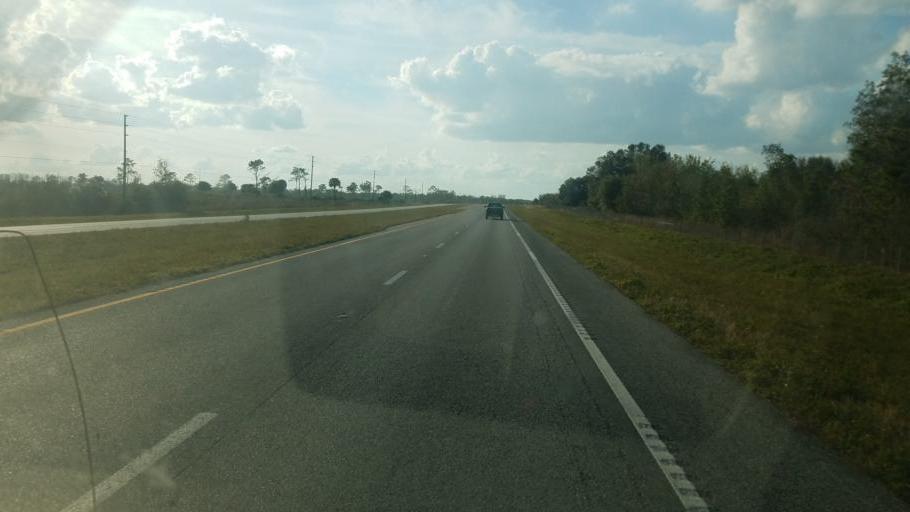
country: US
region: Florida
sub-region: Osceola County
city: Saint Cloud
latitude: 28.1312
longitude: -81.0068
